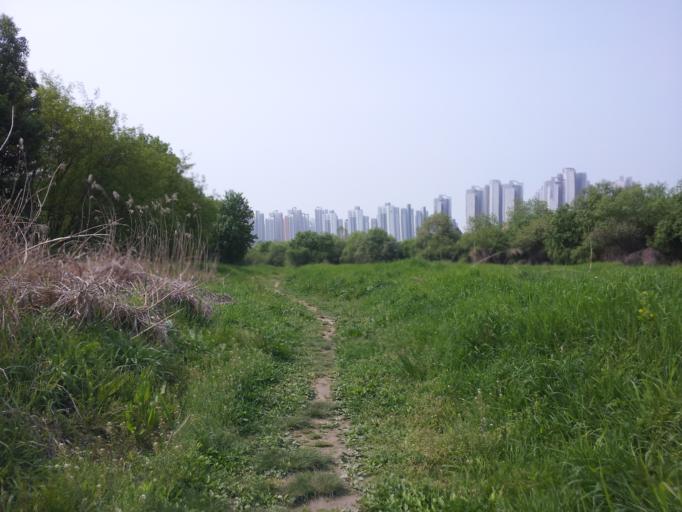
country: KR
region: Daejeon
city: Daejeon
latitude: 36.3221
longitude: 127.3531
